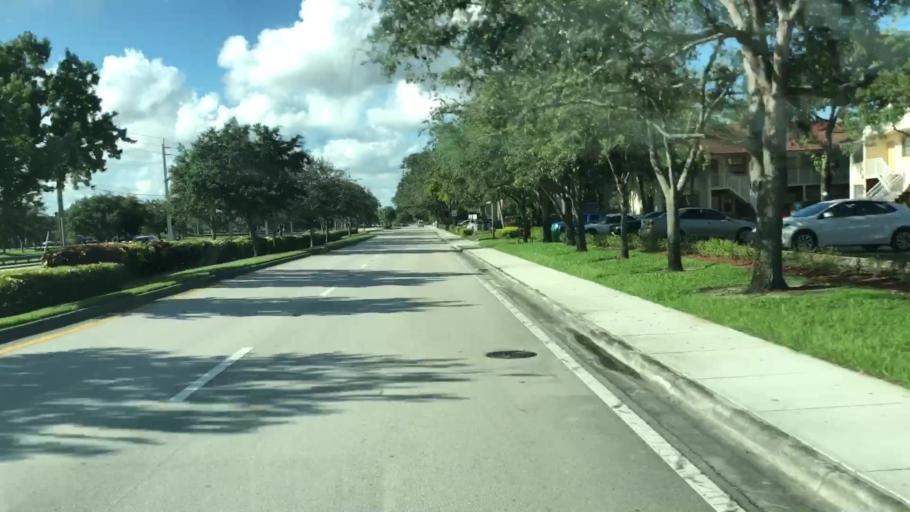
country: US
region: Florida
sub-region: Broward County
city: Coral Springs
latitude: 26.2651
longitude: -80.2663
